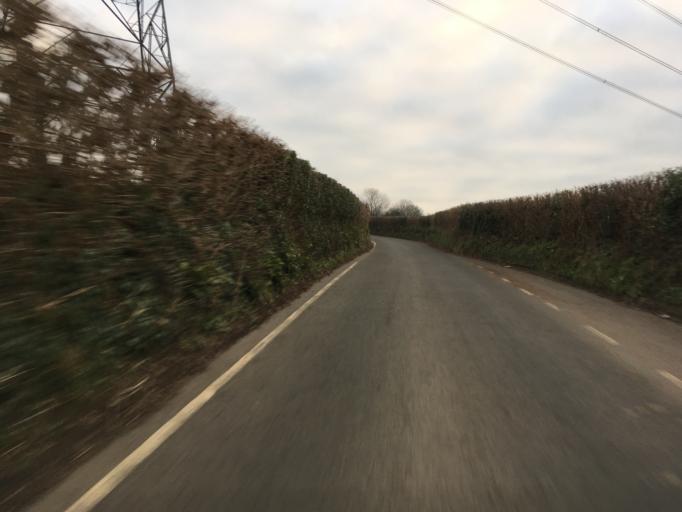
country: GB
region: Wales
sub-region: Newport
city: Marshfield
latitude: 51.5593
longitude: -3.0969
